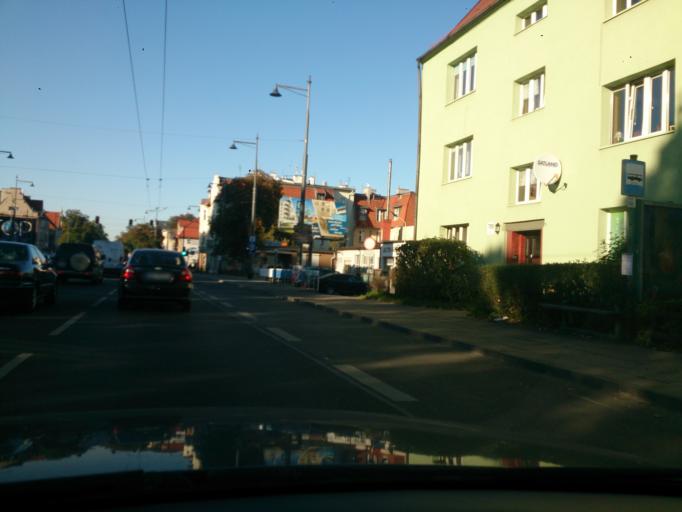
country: PL
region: Pomeranian Voivodeship
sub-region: Sopot
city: Sopot
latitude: 54.4339
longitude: 18.5617
